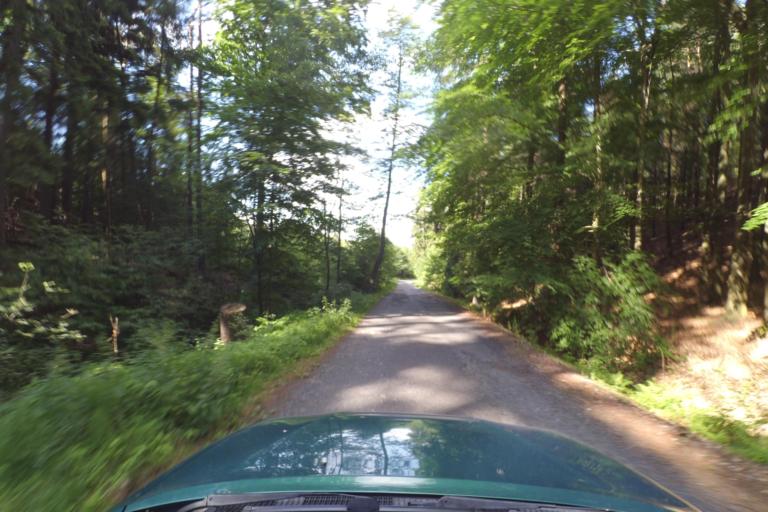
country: CZ
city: Osecna
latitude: 50.6822
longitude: 14.8986
